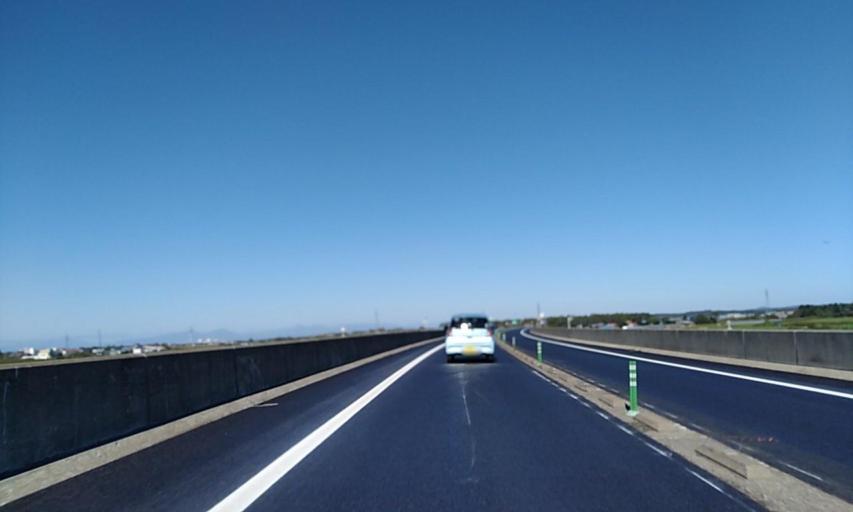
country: JP
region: Hokkaido
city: Tomakomai
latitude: 42.5814
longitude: 141.9467
